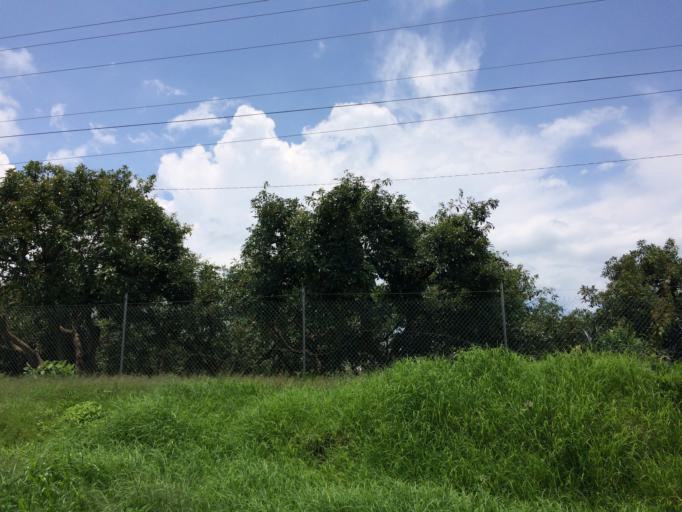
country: MX
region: Michoacan
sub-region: Periban
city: San Francisco Periban
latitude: 19.5578
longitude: -102.3924
